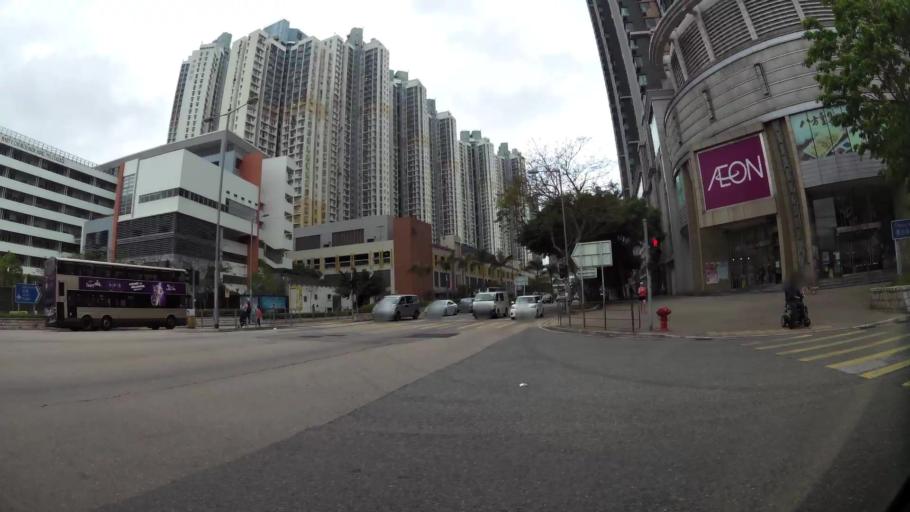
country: HK
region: Sham Shui Po
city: Sham Shui Po
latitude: 22.3317
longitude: 114.1487
